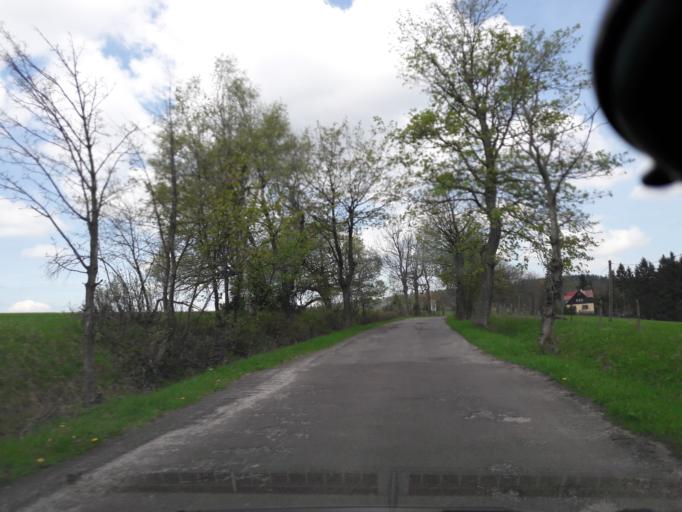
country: PL
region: Lower Silesian Voivodeship
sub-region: Powiat klodzki
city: Duszniki-Zdroj
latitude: 50.4542
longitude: 16.3427
